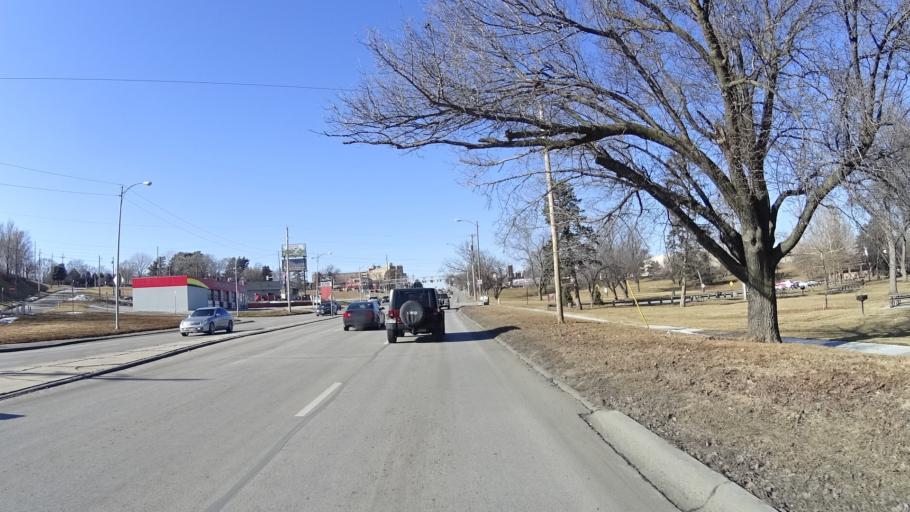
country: US
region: Nebraska
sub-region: Douglas County
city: Omaha
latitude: 41.2960
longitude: -96.0206
